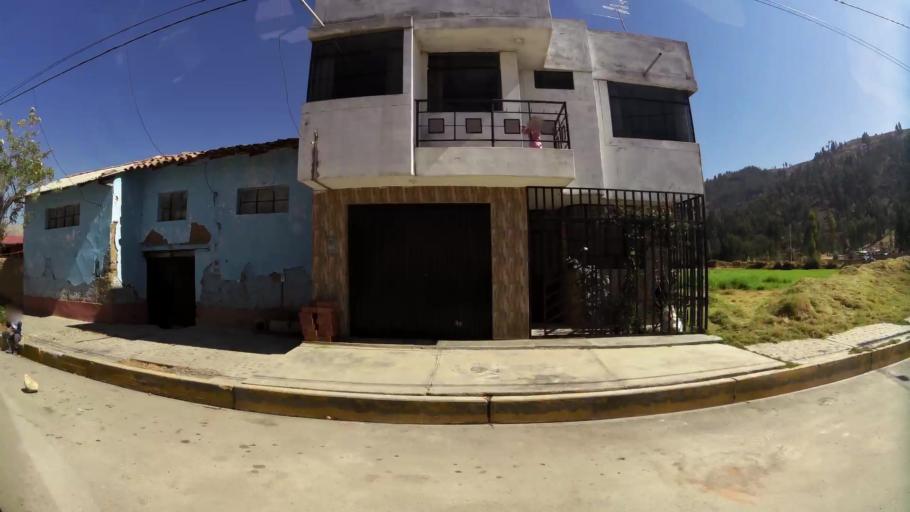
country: PE
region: Junin
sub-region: Provincia de Huancayo
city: San Jeronimo
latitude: -11.9428
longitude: -75.2940
